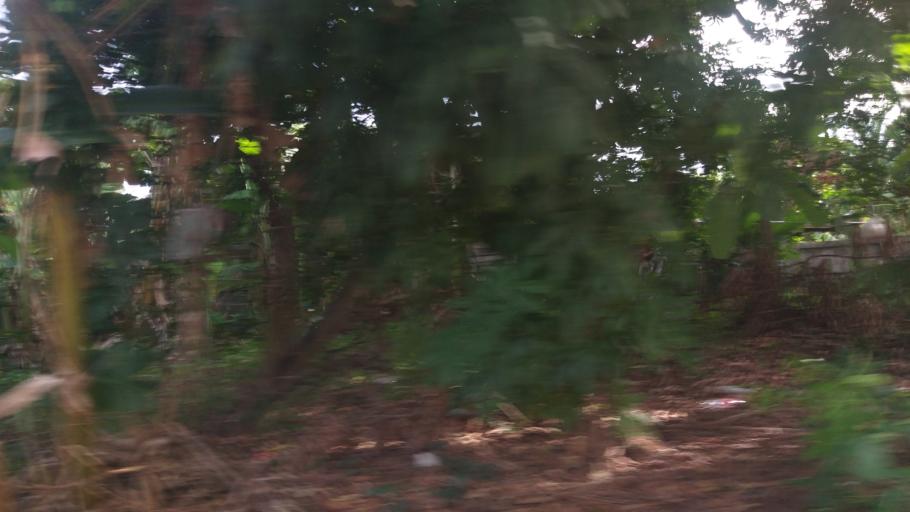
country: TH
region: Chaiyaphum
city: Ban Thaen
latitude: 16.4092
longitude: 102.3496
